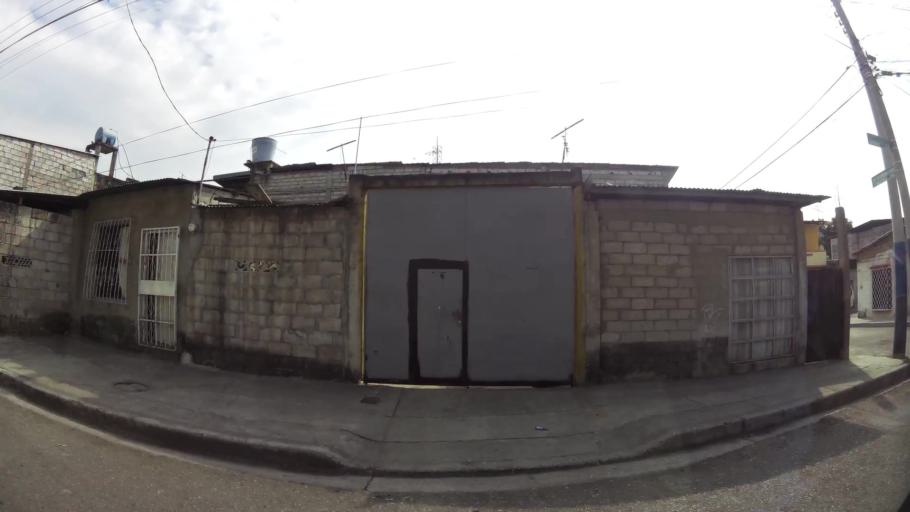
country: EC
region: Guayas
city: Guayaquil
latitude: -2.2524
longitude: -79.9053
